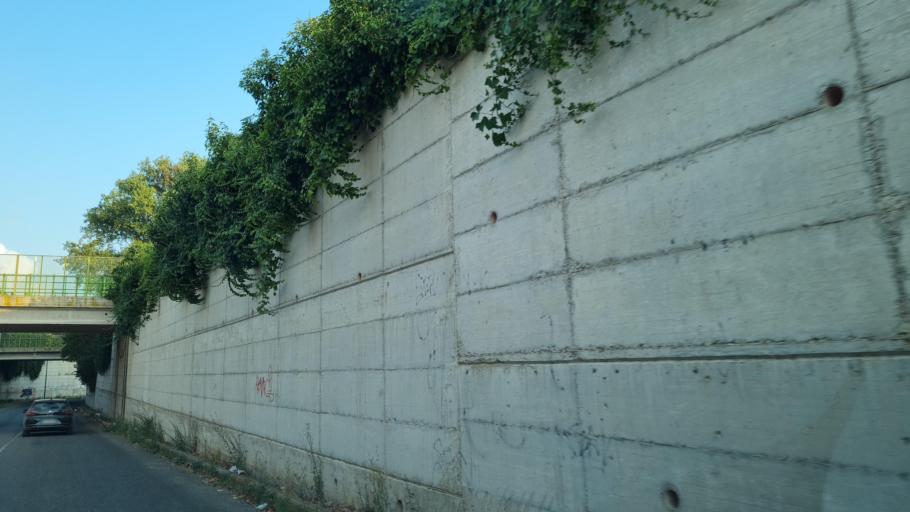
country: IT
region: Latium
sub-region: Provincia di Viterbo
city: Montalto di Castro
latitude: 42.3268
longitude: 11.6178
